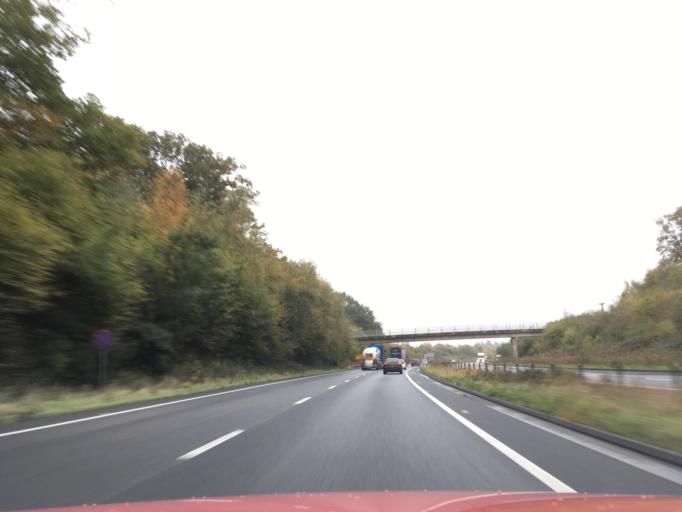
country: GB
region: England
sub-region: Hampshire
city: Highclere
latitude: 51.3772
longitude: -1.3627
